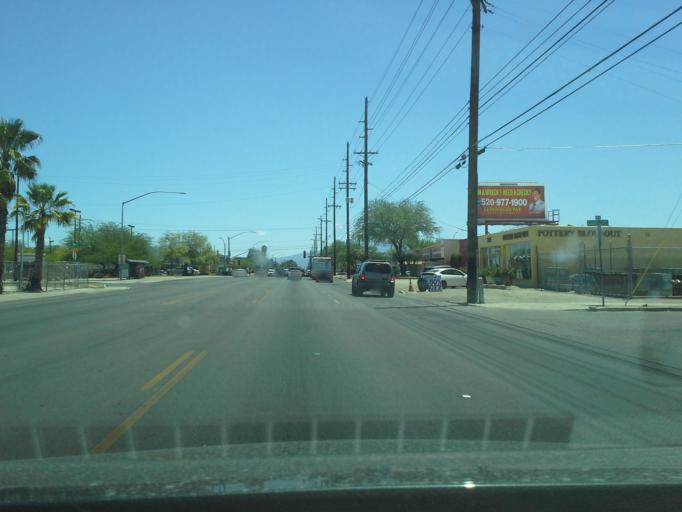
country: US
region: Arizona
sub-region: Pima County
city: Tucson
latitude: 32.2506
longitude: -110.9116
